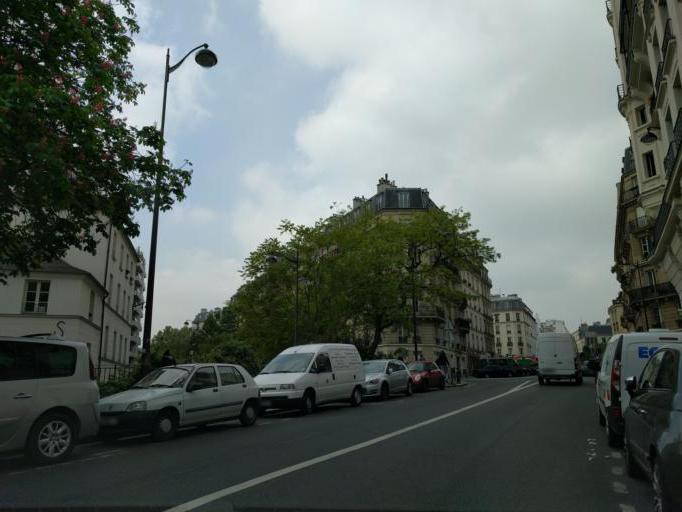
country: FR
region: Ile-de-France
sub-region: Paris
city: Paris
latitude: 48.8406
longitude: 2.3534
